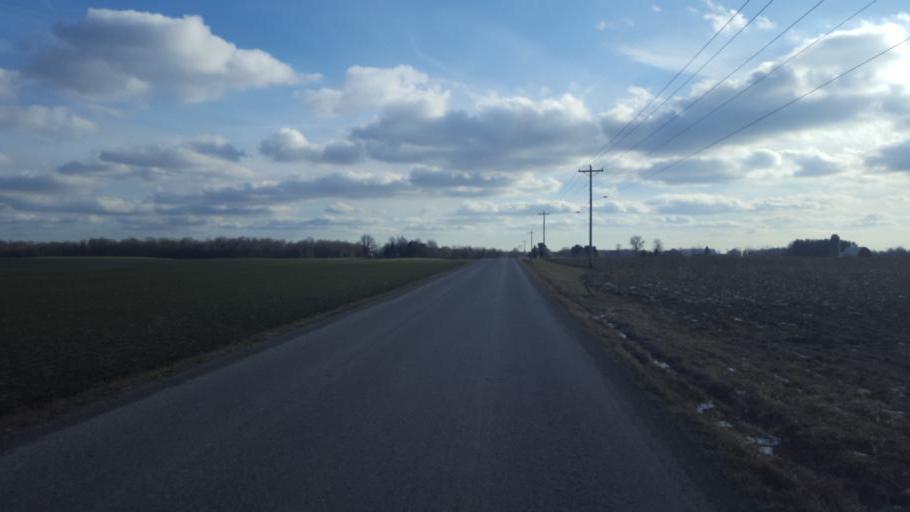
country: US
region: Ohio
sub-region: Morrow County
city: Mount Gilead
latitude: 40.5950
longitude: -82.7288
